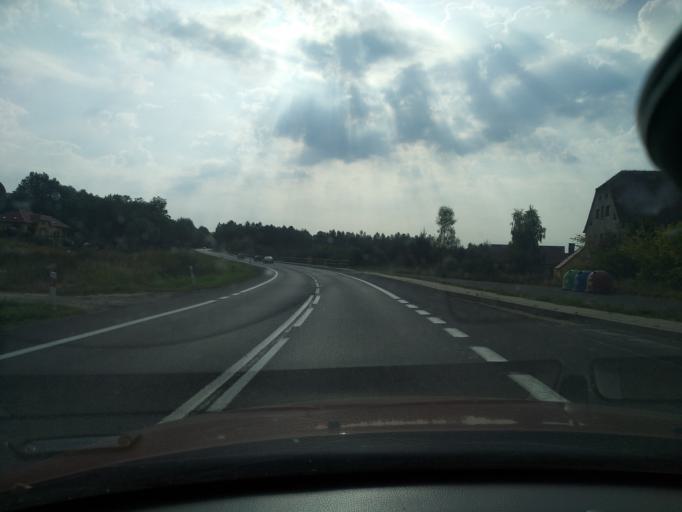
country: PL
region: Lower Silesian Voivodeship
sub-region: Powiat lubanski
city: Olszyna
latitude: 51.0814
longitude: 15.3344
